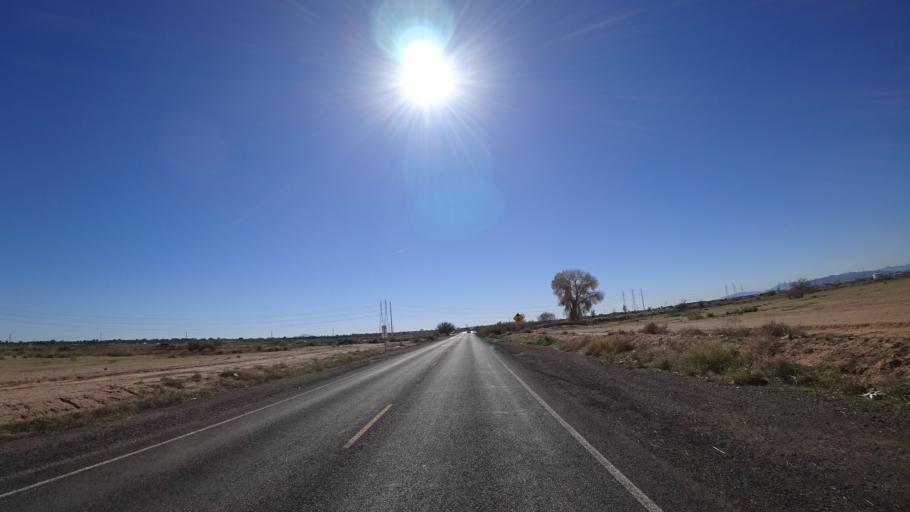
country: US
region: Arizona
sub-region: Maricopa County
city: Mesa
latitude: 33.4557
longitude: -111.8660
